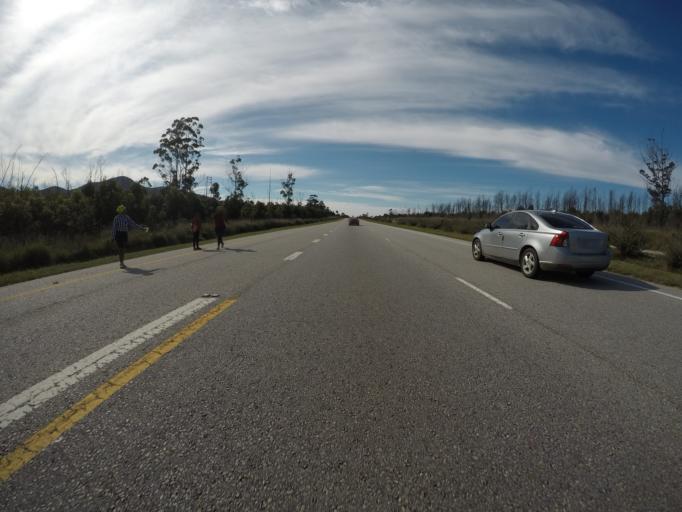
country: ZA
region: Eastern Cape
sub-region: Nelson Mandela Bay Metropolitan Municipality
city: Uitenhage
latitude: -33.9091
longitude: 25.2341
